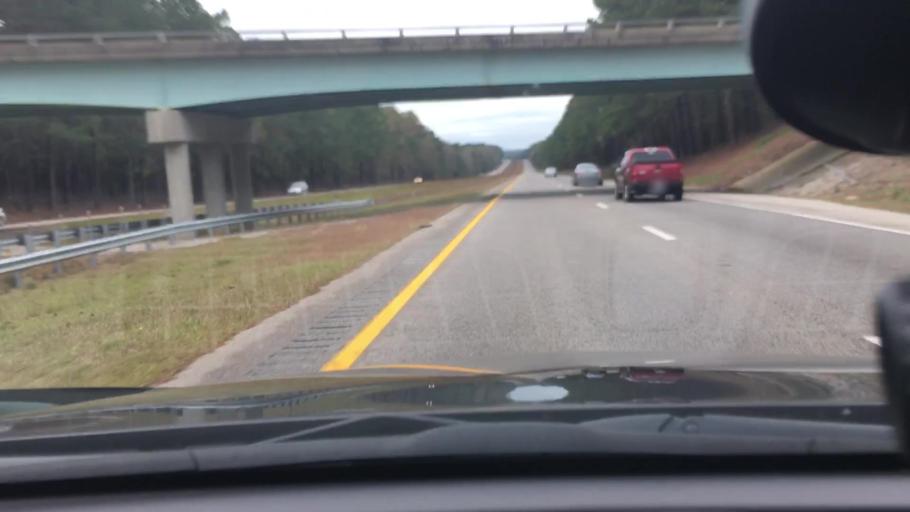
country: US
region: North Carolina
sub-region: Wake County
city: Zebulon
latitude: 35.8101
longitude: -78.2233
